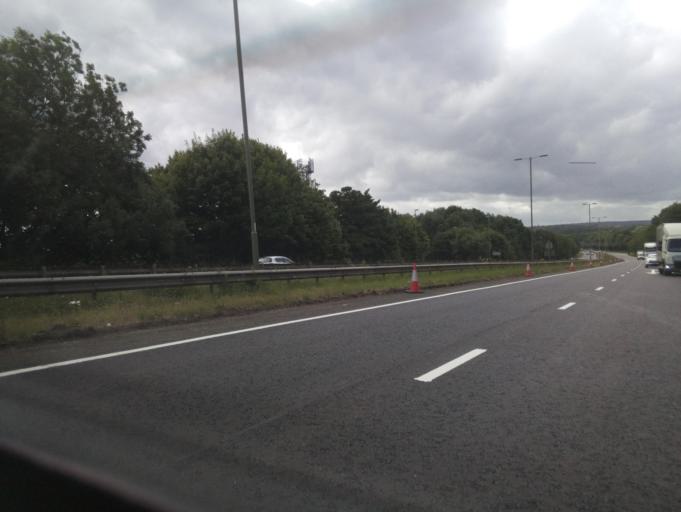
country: GB
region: England
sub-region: Hampshire
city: Basingstoke
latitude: 51.2703
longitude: -1.0699
